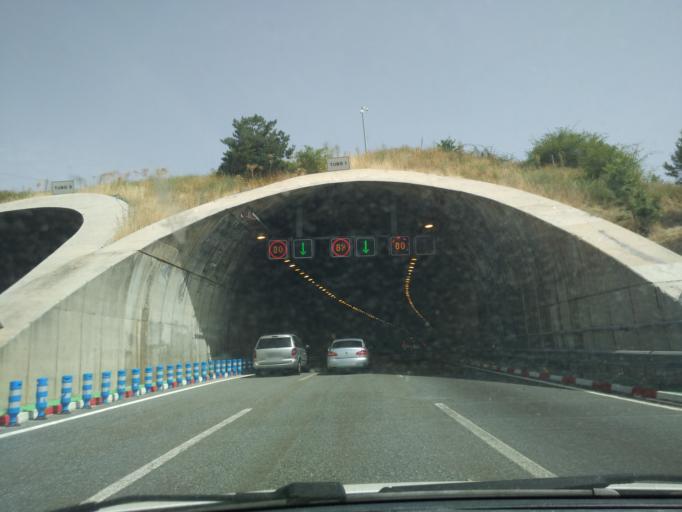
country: ES
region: Madrid
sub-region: Provincia de Madrid
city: Somosierra
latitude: 41.1311
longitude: -3.5839
